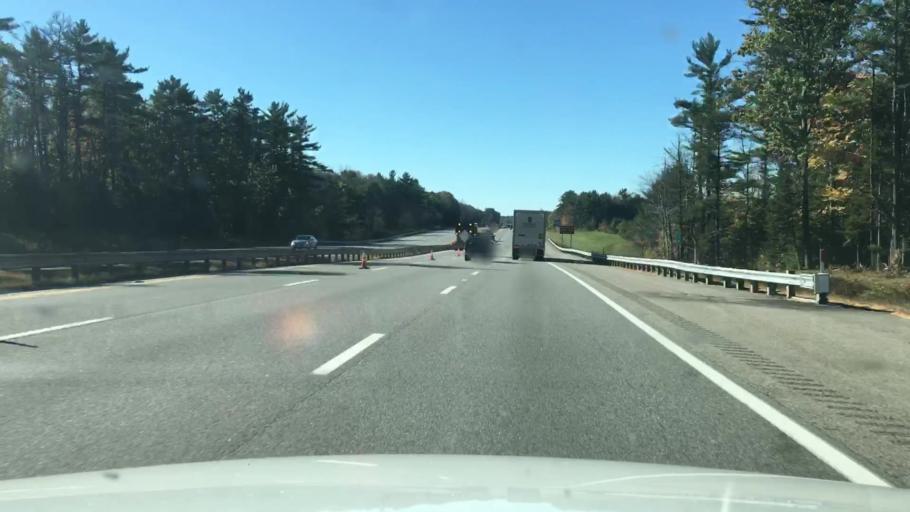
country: US
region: Maine
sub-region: York County
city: West Kennebunk
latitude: 43.4393
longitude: -70.5409
